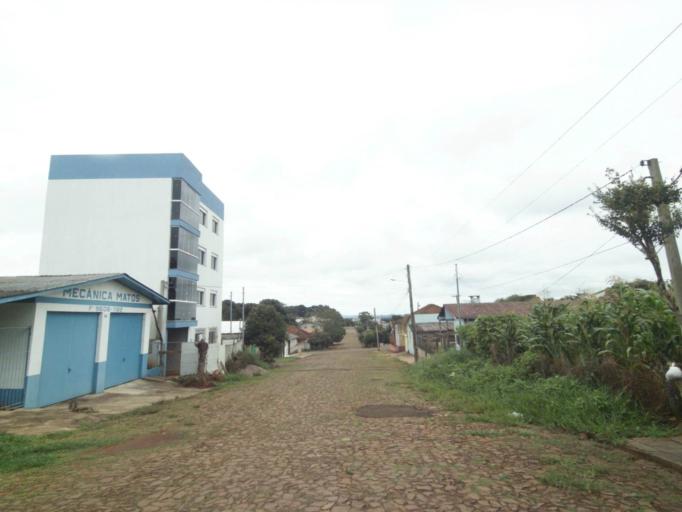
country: BR
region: Rio Grande do Sul
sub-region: Lagoa Vermelha
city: Lagoa Vermelha
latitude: -28.2179
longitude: -51.5207
